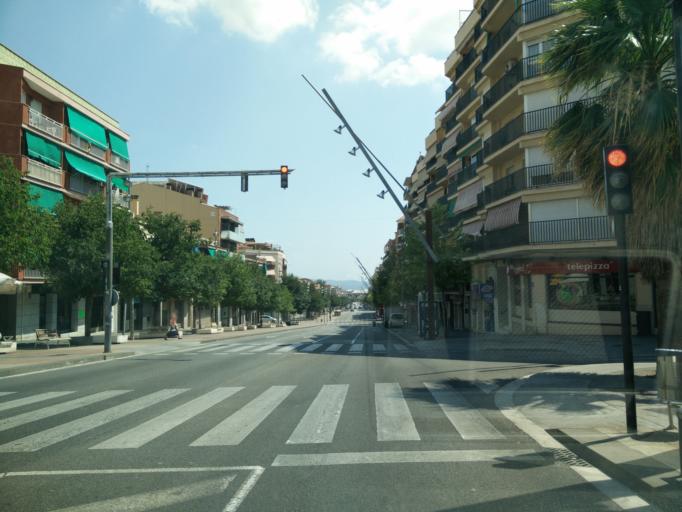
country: ES
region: Catalonia
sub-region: Provincia de Barcelona
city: Terrassa
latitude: 41.5667
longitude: 2.0266
